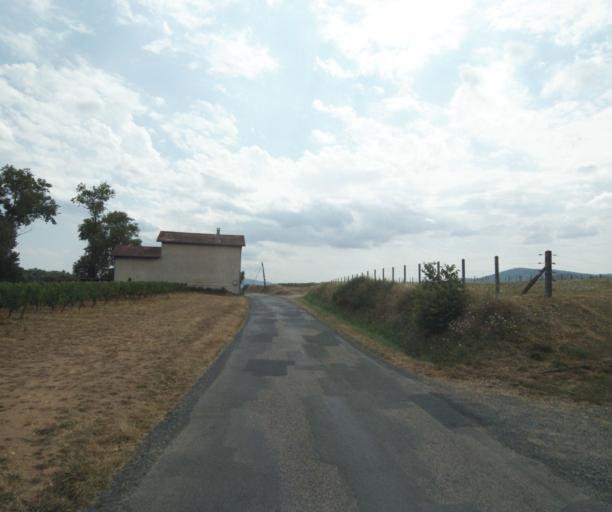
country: FR
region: Rhone-Alpes
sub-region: Departement du Rhone
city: Bully
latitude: 45.8648
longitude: 4.5769
